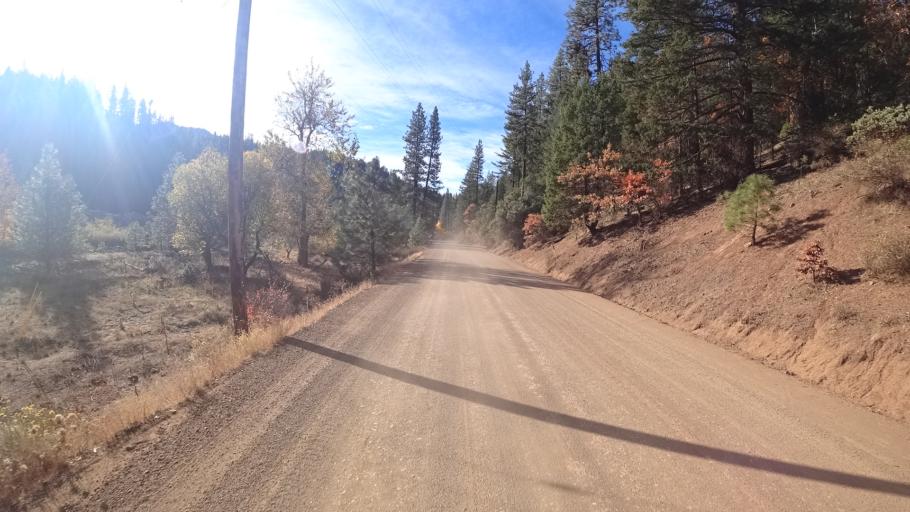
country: US
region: California
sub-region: Siskiyou County
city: Yreka
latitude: 41.6898
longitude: -122.8185
